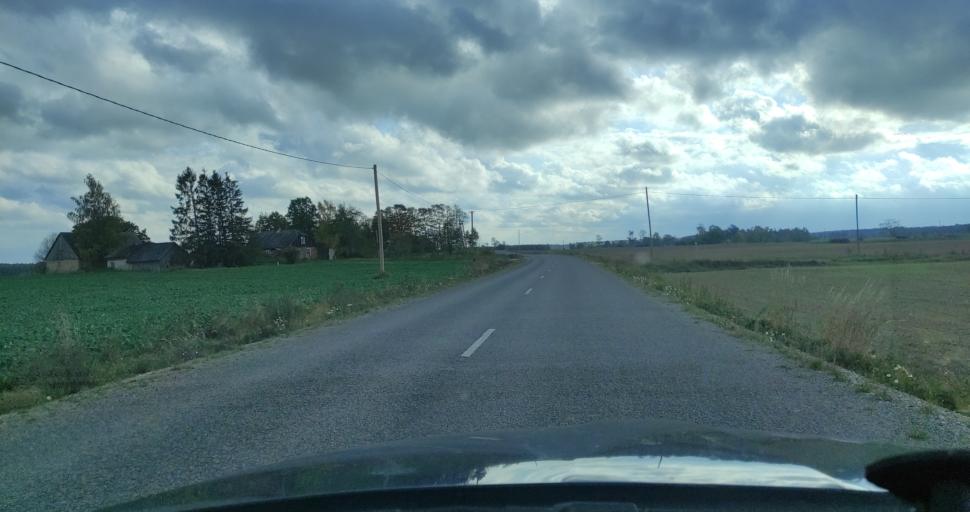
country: LV
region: Talsu Rajons
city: Sabile
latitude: 56.9380
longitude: 22.3965
